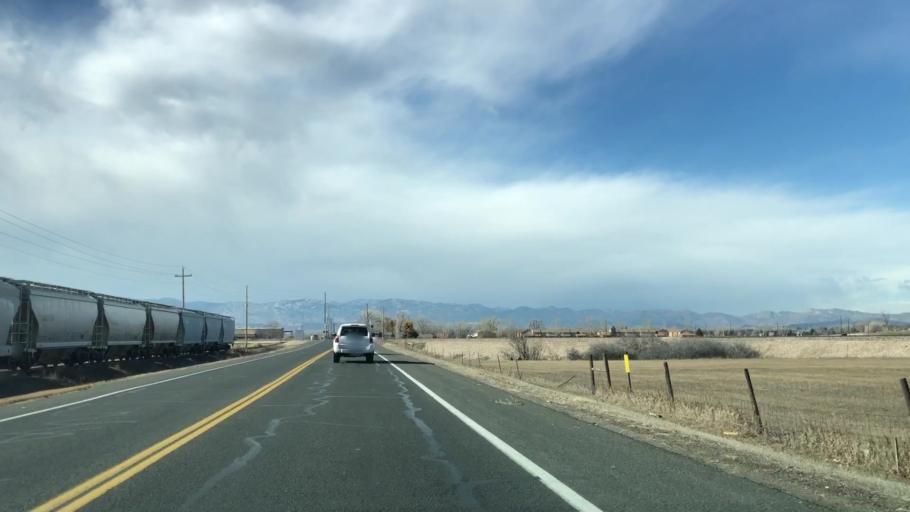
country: US
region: Colorado
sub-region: Larimer County
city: Fort Collins
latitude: 40.5960
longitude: -105.0224
